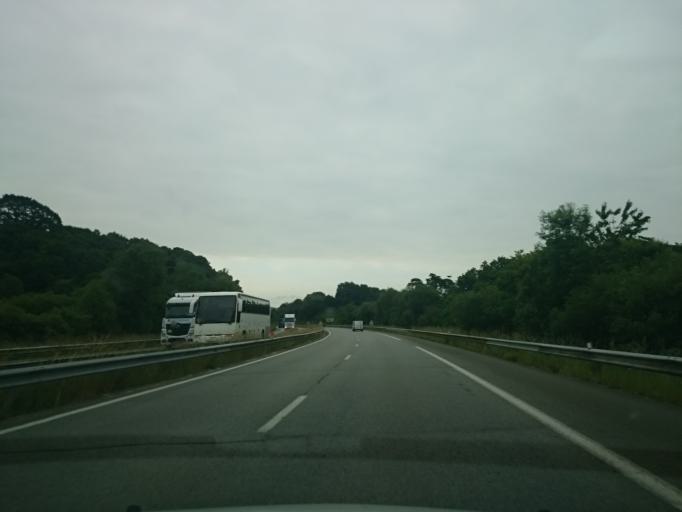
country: FR
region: Brittany
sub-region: Departement du Finistere
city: Dineault
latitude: 48.2539
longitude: -4.1149
